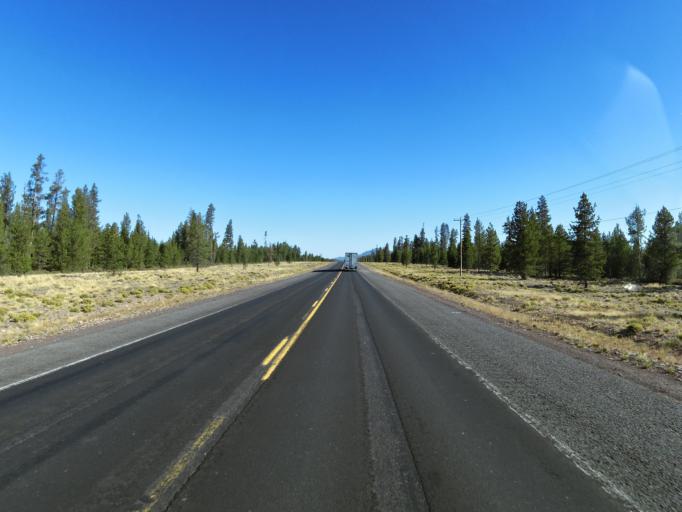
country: US
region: Oregon
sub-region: Deschutes County
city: La Pine
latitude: 43.1417
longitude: -121.7998
